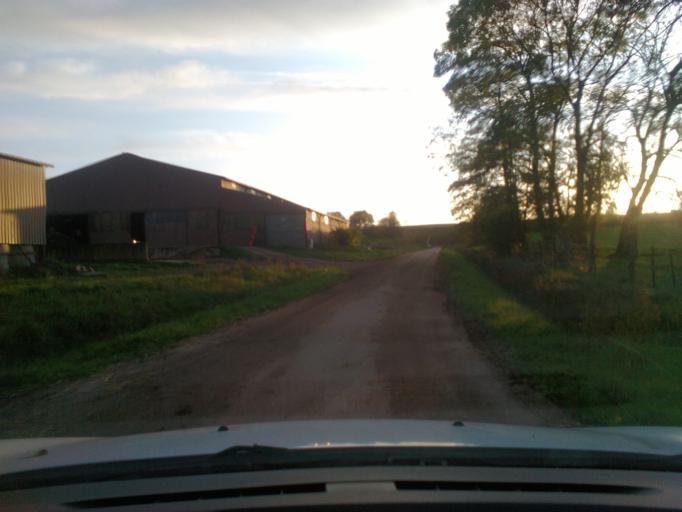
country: FR
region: Lorraine
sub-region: Departement des Vosges
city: Mirecourt
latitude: 48.2569
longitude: 6.1728
